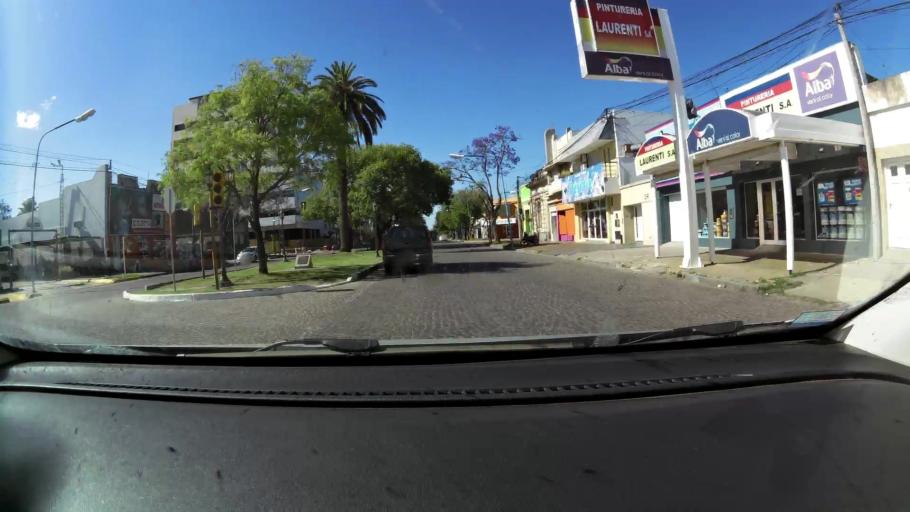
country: AR
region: Santa Fe
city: Rafaela
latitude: -31.2487
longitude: -61.4907
